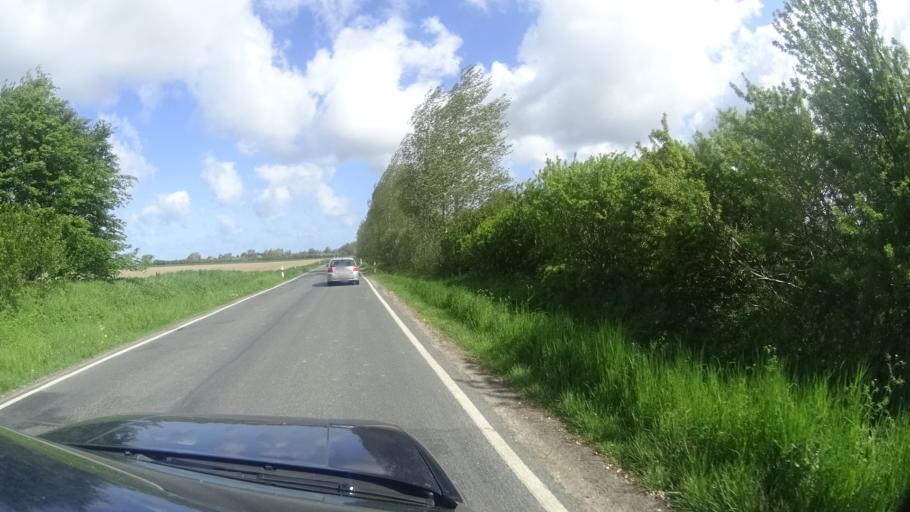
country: DE
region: Mecklenburg-Vorpommern
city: Trinwillershagen
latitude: 54.3055
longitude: 12.5849
